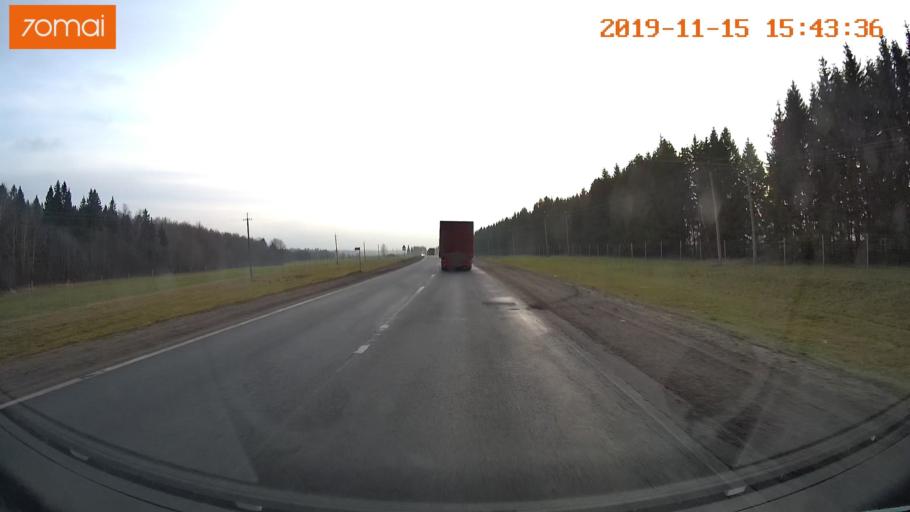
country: RU
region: Jaroslavl
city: Danilov
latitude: 57.9802
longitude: 40.0267
